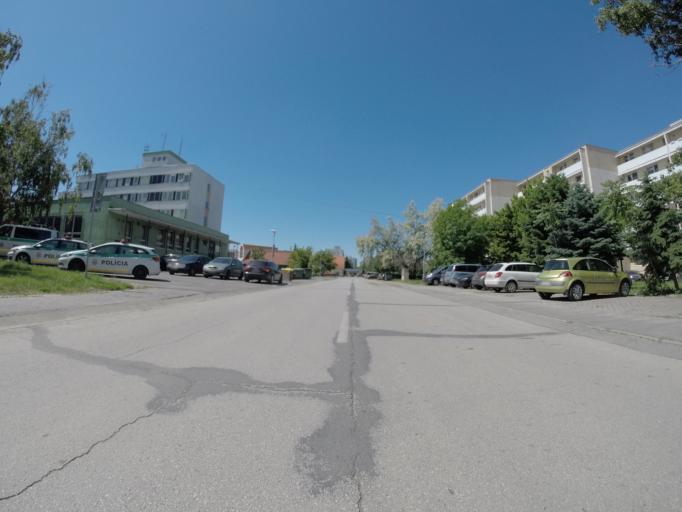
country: SK
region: Trnavsky
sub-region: Okres Galanta
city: Galanta
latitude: 48.1917
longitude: 17.7291
